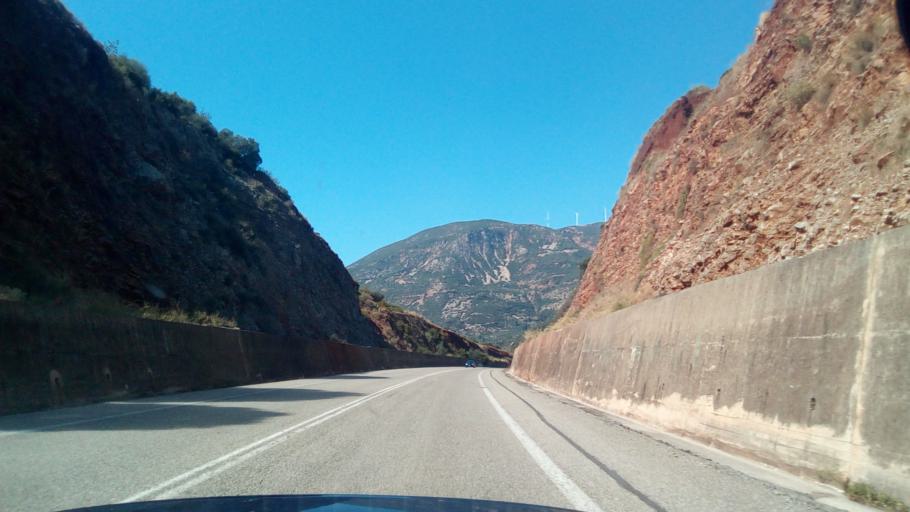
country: GR
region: West Greece
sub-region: Nomos Achaias
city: Selianitika
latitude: 38.3893
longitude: 22.0764
